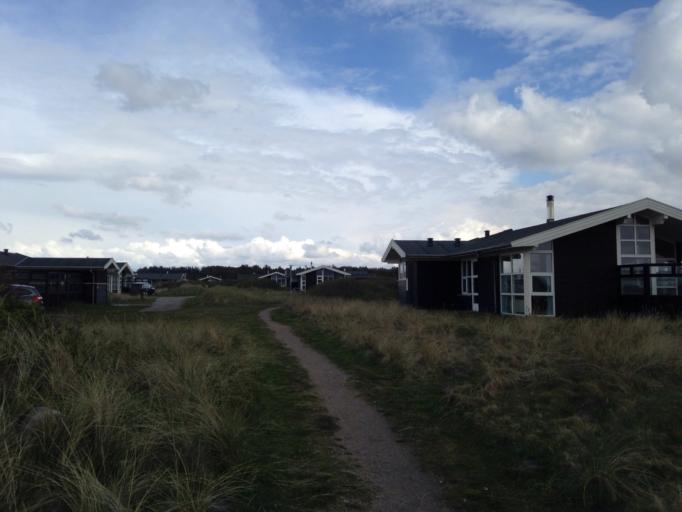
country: DK
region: North Denmark
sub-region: Hjorring Kommune
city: Hjorring
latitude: 57.4925
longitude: 9.8296
